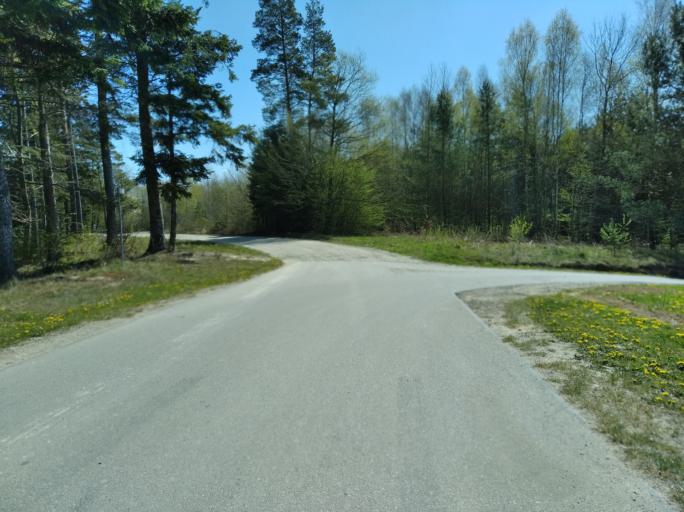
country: PL
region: Subcarpathian Voivodeship
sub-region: Powiat brzozowski
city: Dydnia
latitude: 49.7208
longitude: 22.1619
